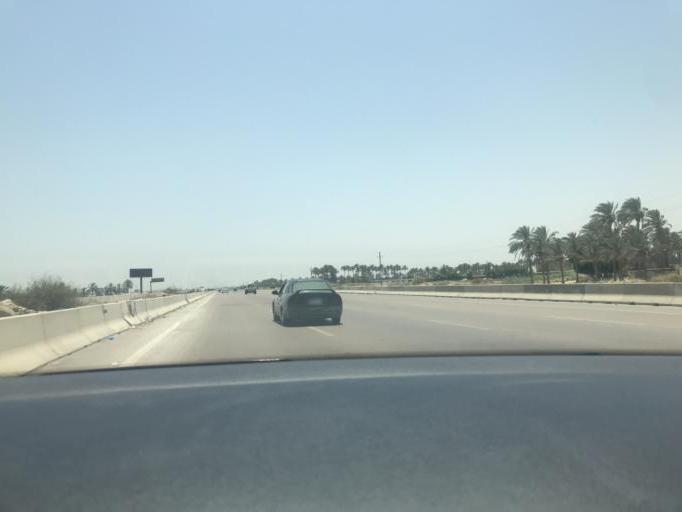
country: EG
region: Al Buhayrah
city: Abu al Matamir
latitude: 30.8743
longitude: 29.8880
